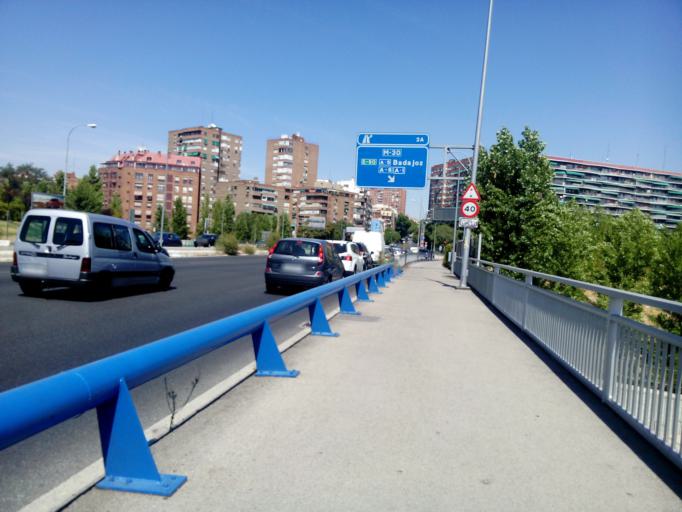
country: ES
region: Madrid
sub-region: Provincia de Madrid
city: Usera
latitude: 40.3953
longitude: -3.7042
